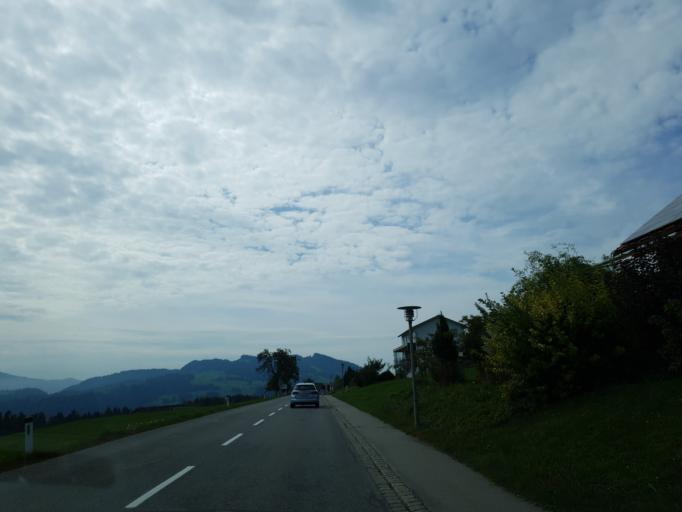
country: AT
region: Vorarlberg
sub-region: Politischer Bezirk Bregenz
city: Doren
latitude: 47.4898
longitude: 9.8689
